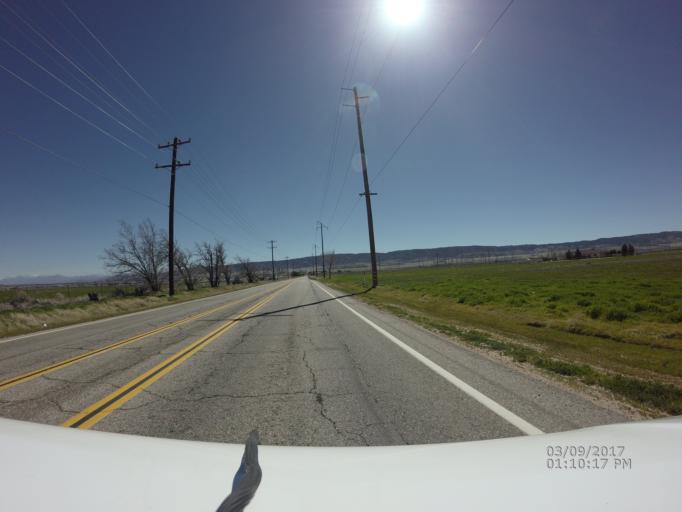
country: US
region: California
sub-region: Los Angeles County
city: Leona Valley
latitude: 34.6991
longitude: -118.2894
